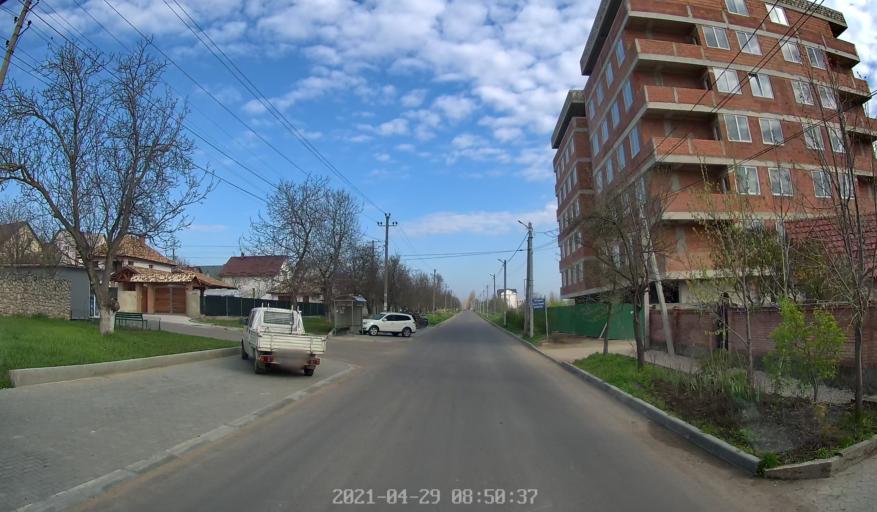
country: MD
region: Chisinau
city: Cricova
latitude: 47.1312
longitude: 28.8617
